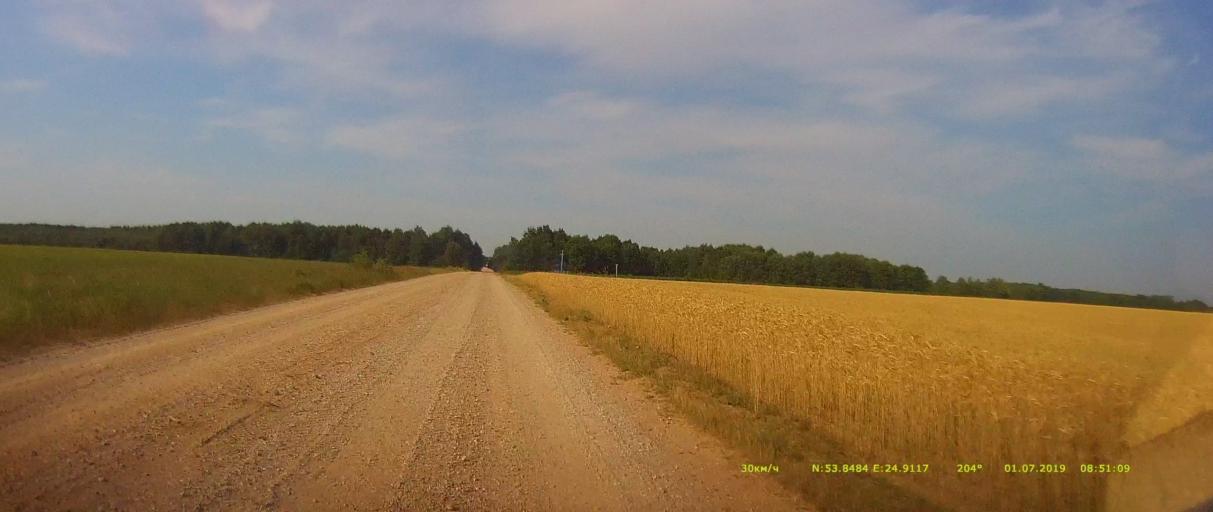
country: BY
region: Grodnenskaya
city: Shchuchin
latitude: 53.8486
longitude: 24.9118
